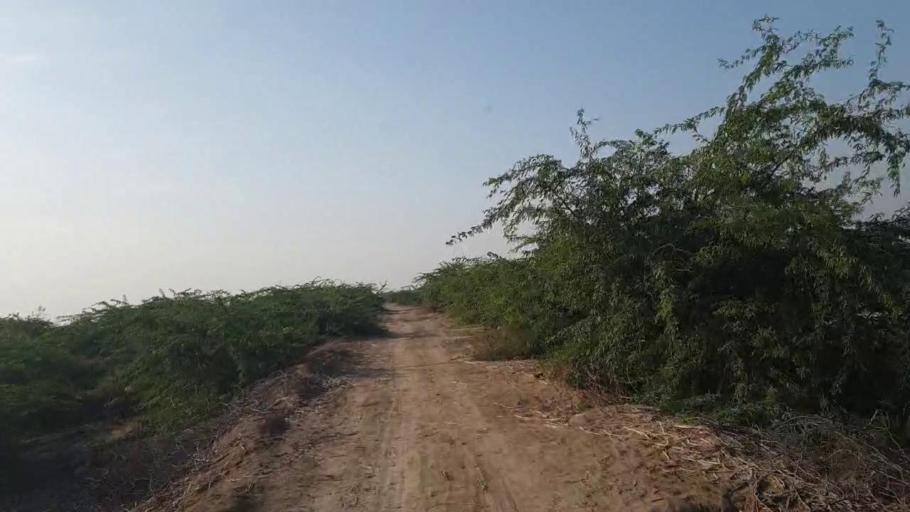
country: PK
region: Sindh
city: Badin
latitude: 24.4520
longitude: 68.7328
